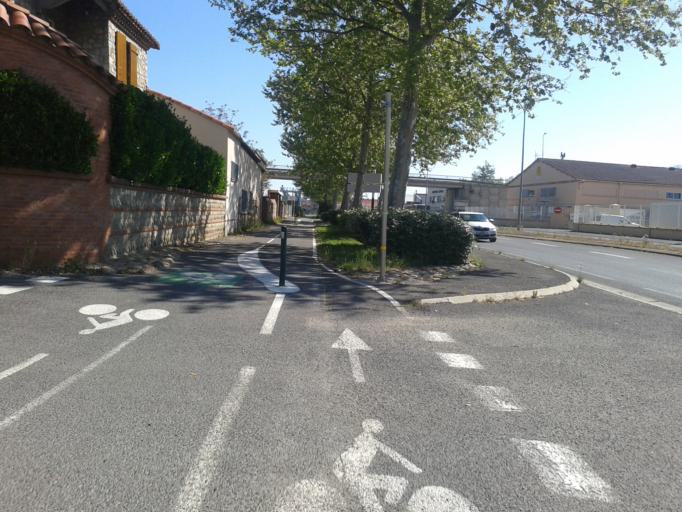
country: FR
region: Languedoc-Roussillon
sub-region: Departement des Pyrenees-Orientales
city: Perpignan
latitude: 42.6878
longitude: 2.8725
